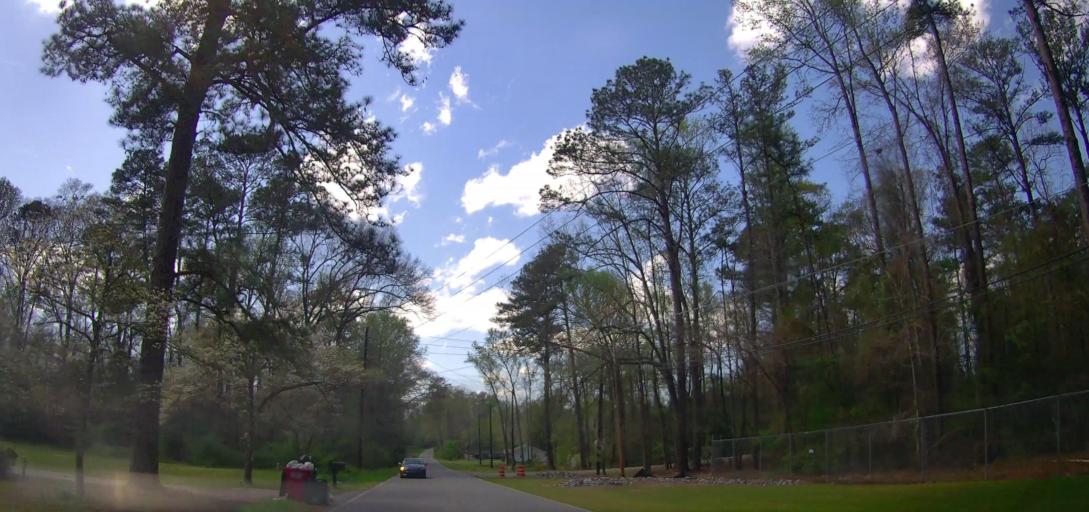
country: US
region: Georgia
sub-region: Bibb County
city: Macon
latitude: 32.8164
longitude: -83.5470
